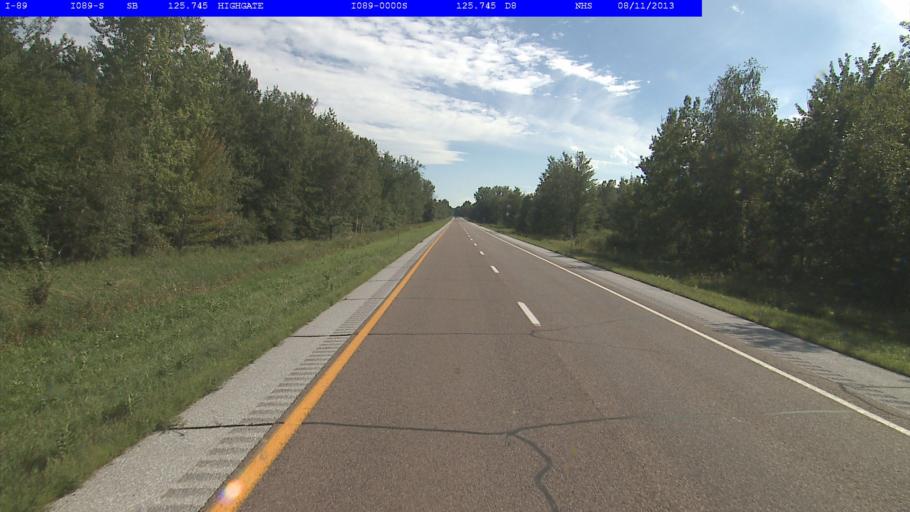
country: US
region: Vermont
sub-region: Franklin County
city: Swanton
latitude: 44.9554
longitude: -73.1107
